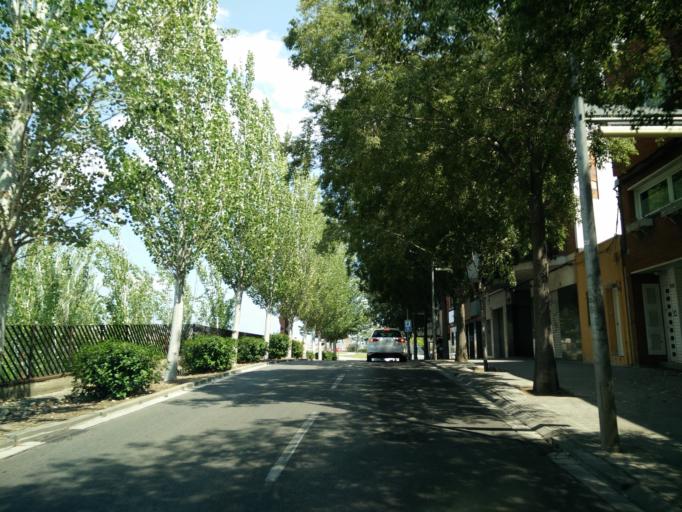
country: ES
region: Catalonia
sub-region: Provincia de Barcelona
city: Terrassa
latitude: 41.5688
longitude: 2.0245
